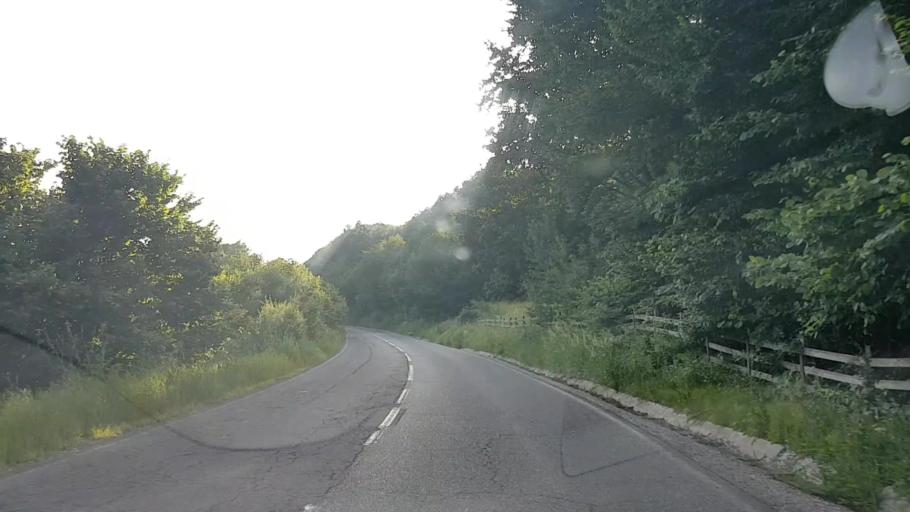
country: RO
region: Harghita
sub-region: Comuna Praid
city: Ocna de Sus
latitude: 46.5732
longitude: 25.2047
